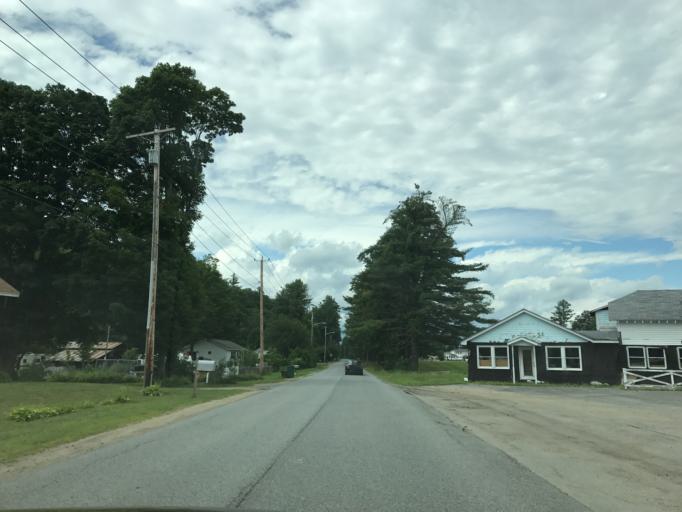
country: US
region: New York
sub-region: Saratoga County
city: Hadley
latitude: 43.3004
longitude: -73.8332
